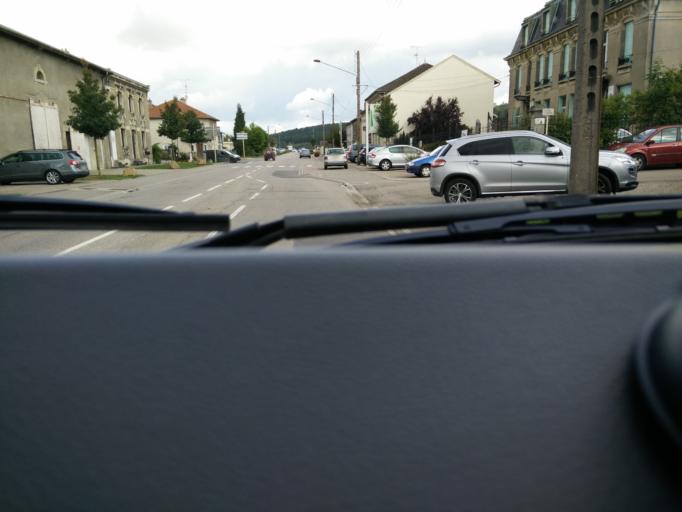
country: FR
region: Lorraine
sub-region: Departement de la Meuse
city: Belleville-sur-Meuse
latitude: 49.2104
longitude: 5.3755
